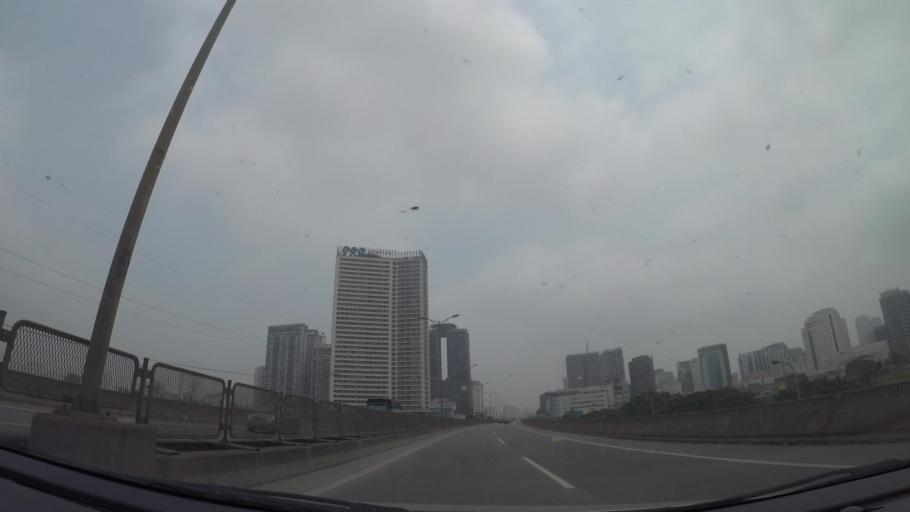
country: VN
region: Ha Noi
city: Cau Dien
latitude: 21.0249
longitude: 105.7787
